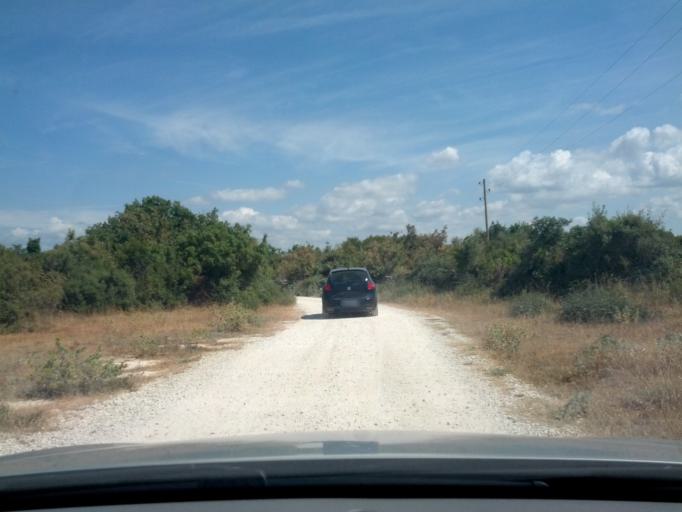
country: HR
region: Istarska
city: Fazana
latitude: 44.9792
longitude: 13.7886
